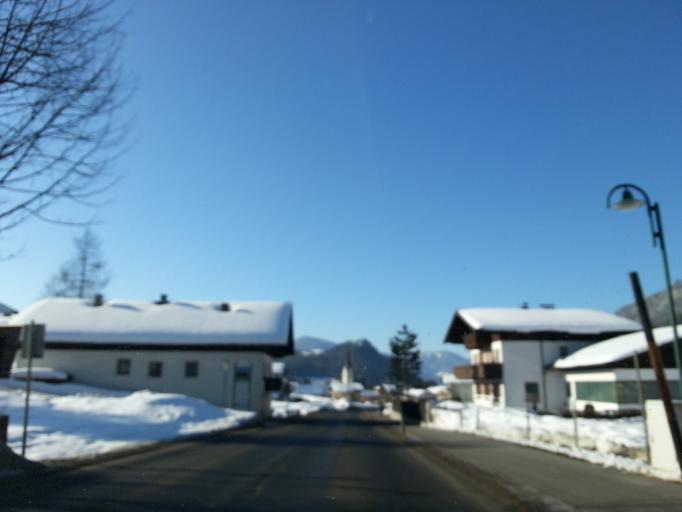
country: AT
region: Salzburg
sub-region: Politischer Bezirk Sankt Johann im Pongau
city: Eben im Pongau
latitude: 47.4688
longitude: 13.3833
